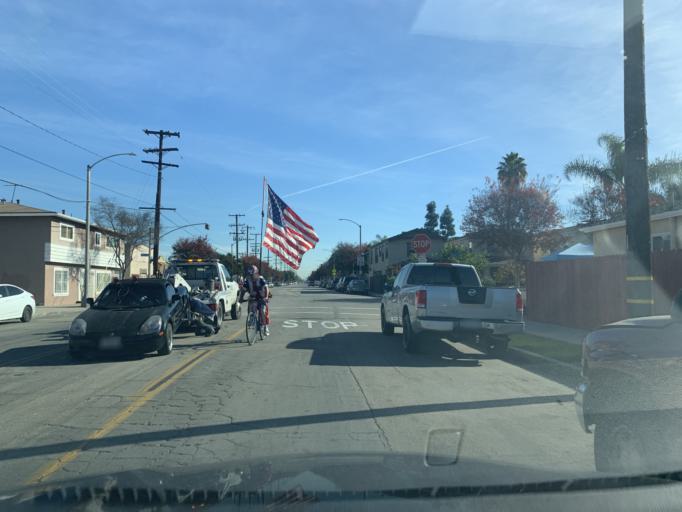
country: US
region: California
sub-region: Los Angeles County
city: East Rancho Dominguez
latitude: 33.8600
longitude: -118.1919
